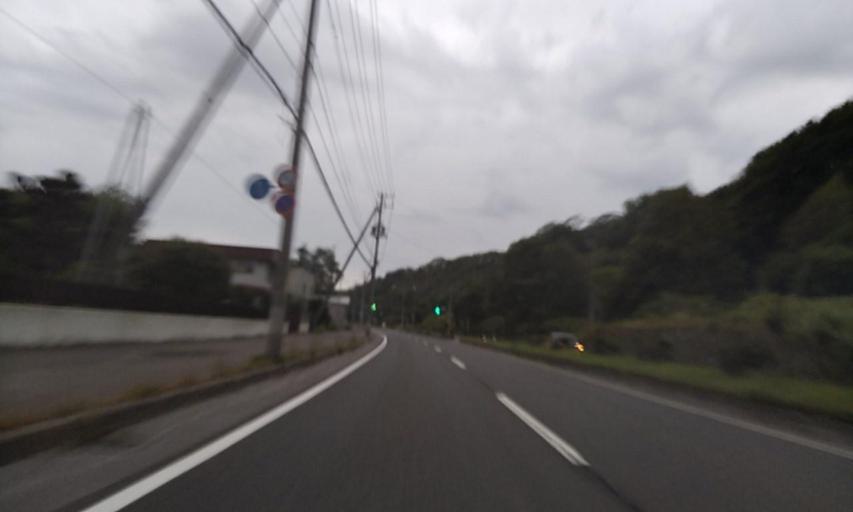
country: JP
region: Hokkaido
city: Abashiri
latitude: 43.9843
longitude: 144.2960
